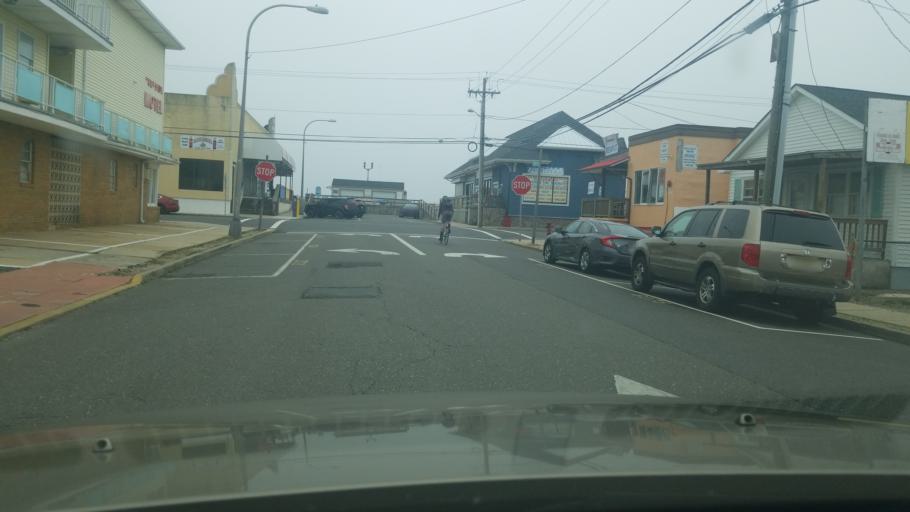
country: US
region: New Jersey
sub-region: Ocean County
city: Seaside Heights
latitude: 39.9389
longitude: -74.0725
